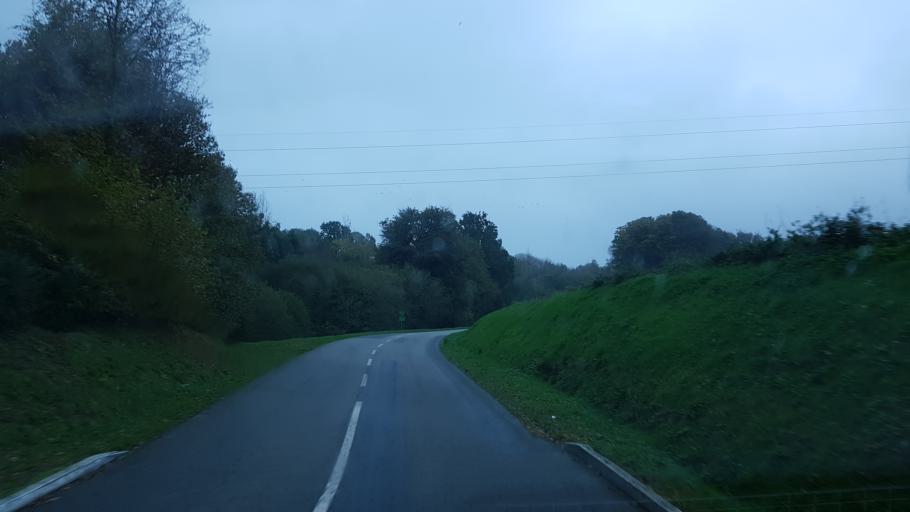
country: FR
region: Brittany
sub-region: Departement du Morbihan
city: Sulniac
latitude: 47.6804
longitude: -2.5713
